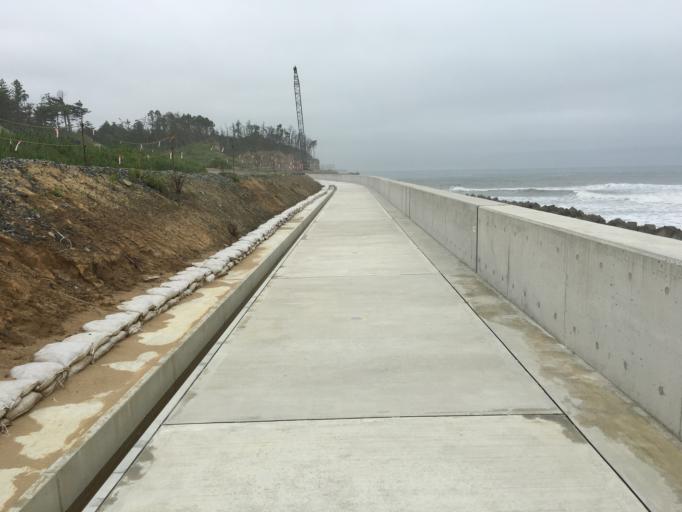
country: JP
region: Fukushima
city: Namie
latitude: 37.7453
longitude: 141.0093
